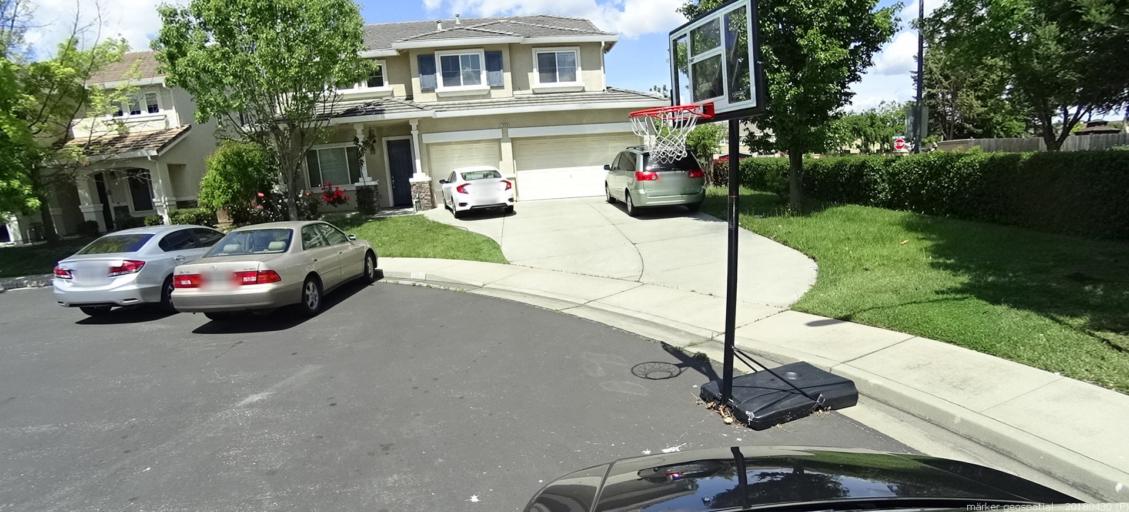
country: US
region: California
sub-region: Yolo County
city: West Sacramento
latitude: 38.5465
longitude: -121.5243
